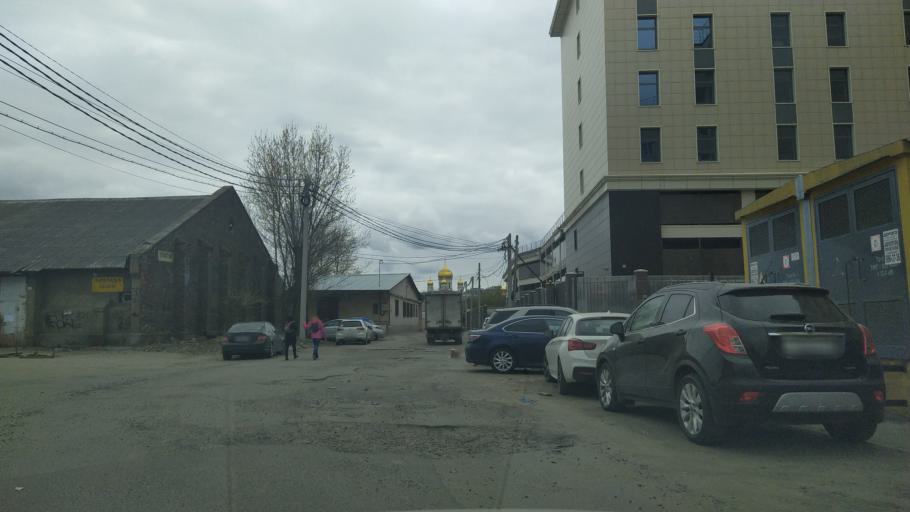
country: RU
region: St.-Petersburg
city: Saint Petersburg
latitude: 59.9022
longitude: 30.3263
